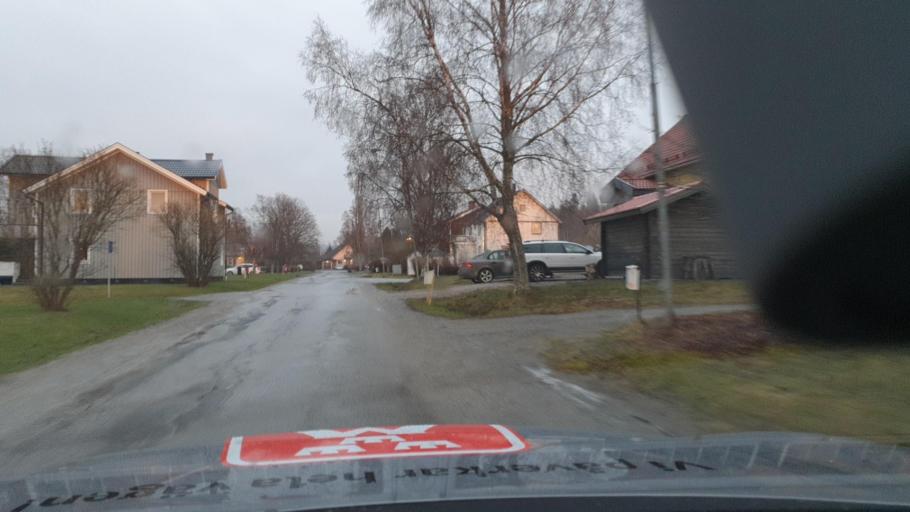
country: SE
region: Vaesternorrland
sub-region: OErnskoeldsviks Kommun
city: Ornskoldsvik
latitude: 63.2719
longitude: 18.6653
